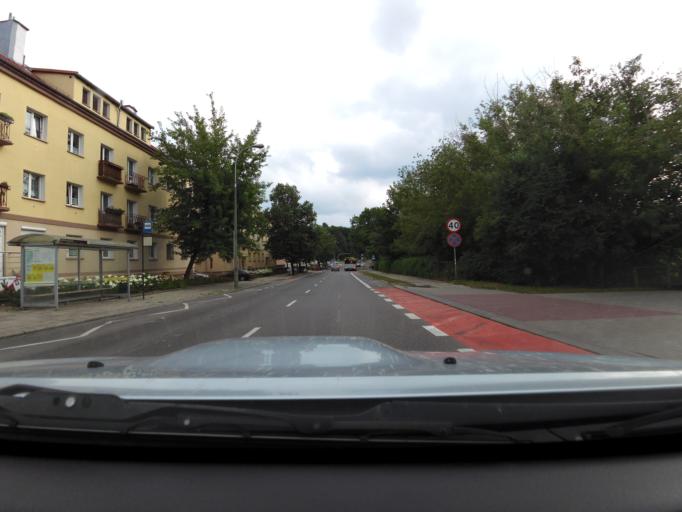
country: PL
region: Warmian-Masurian Voivodeship
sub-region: Powiat olsztynski
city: Olsztyn
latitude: 53.7709
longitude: 20.4835
